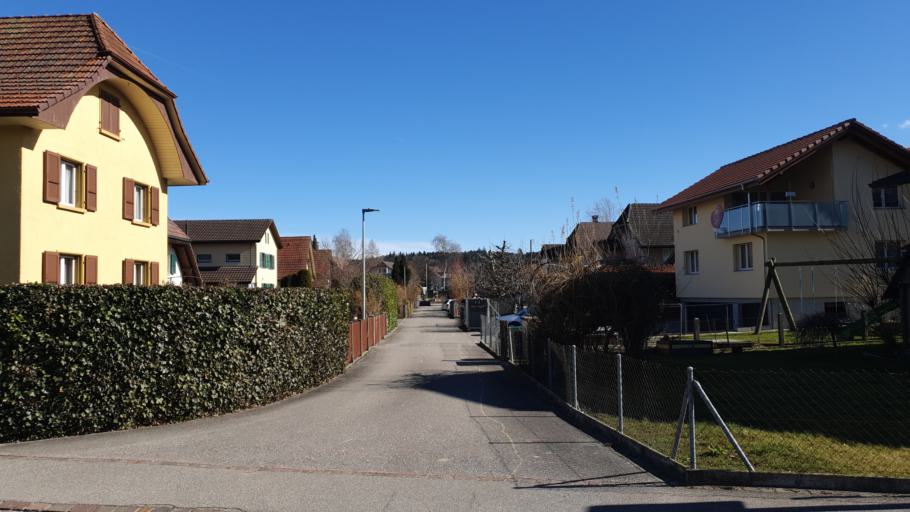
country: CH
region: Bern
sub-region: Oberaargau
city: Lotzwil
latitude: 47.1891
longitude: 7.7845
